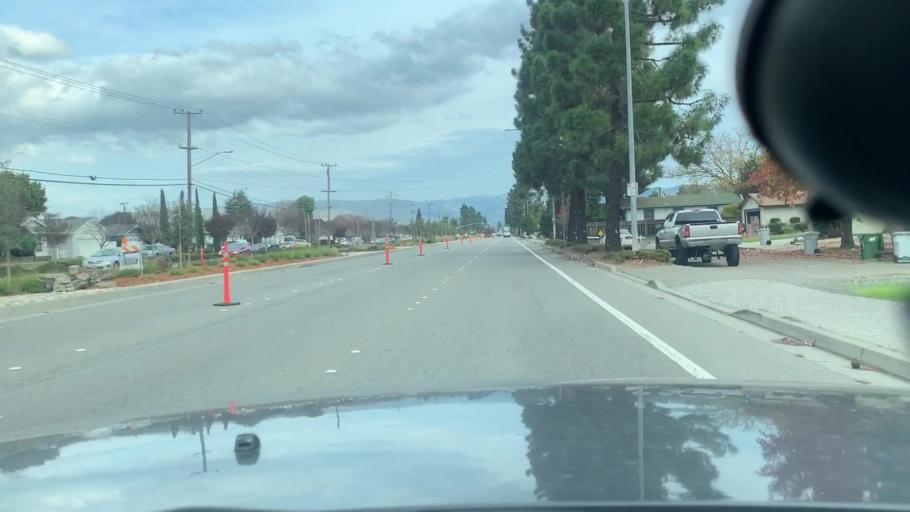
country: US
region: California
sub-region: Alameda County
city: Fremont
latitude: 37.5393
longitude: -121.9958
